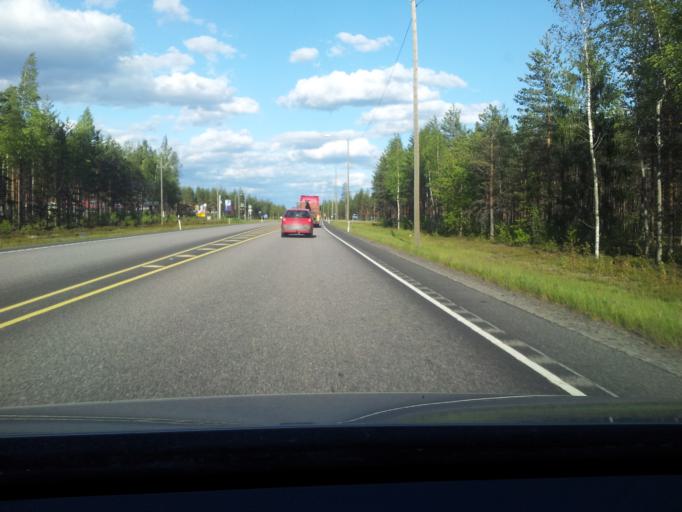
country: FI
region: Kymenlaakso
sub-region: Kouvola
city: Anjala
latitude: 60.9051
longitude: 27.0083
